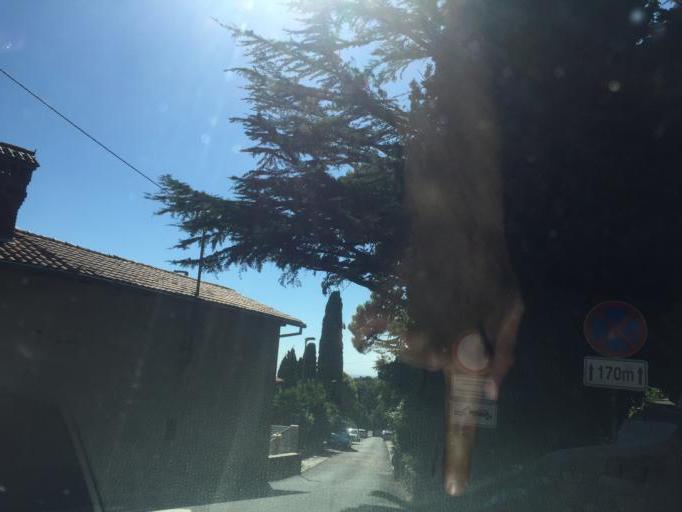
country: SI
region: Piran-Pirano
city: Piran
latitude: 45.5266
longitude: 13.5736
